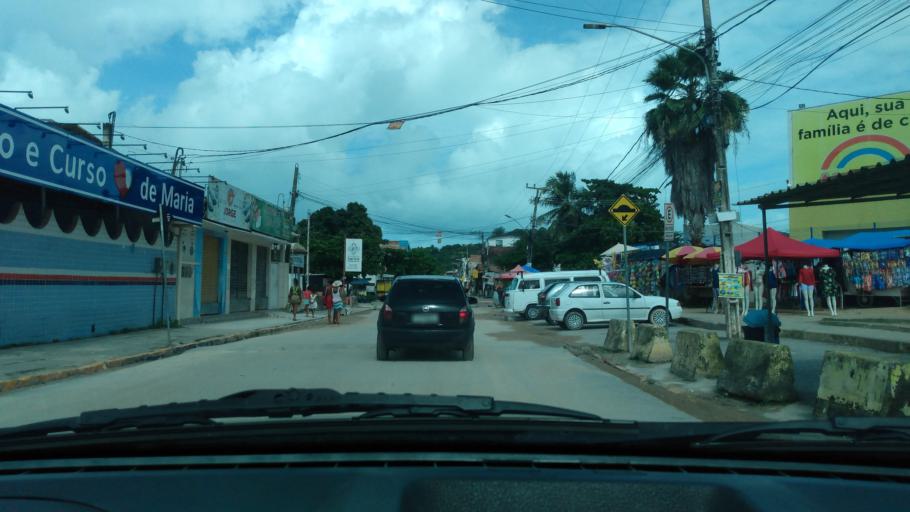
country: BR
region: Pernambuco
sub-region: Cabo De Santo Agostinho
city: Cabo
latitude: -8.3379
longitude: -34.9534
